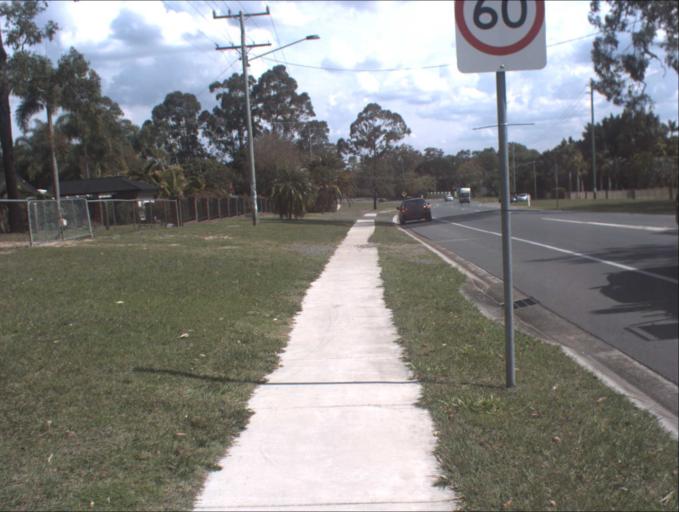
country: AU
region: Queensland
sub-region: Logan
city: Park Ridge South
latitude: -27.6975
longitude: 153.0126
